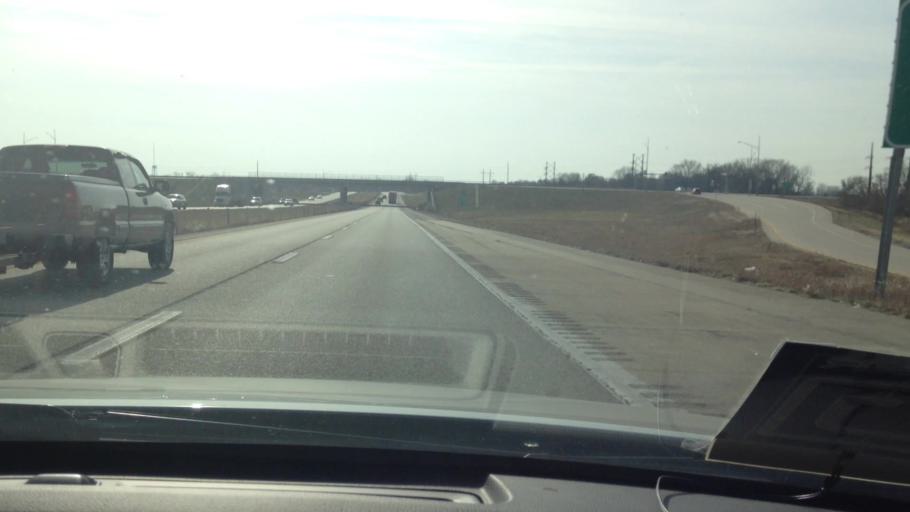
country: US
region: Missouri
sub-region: Cass County
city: Belton
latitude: 38.7888
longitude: -94.4974
